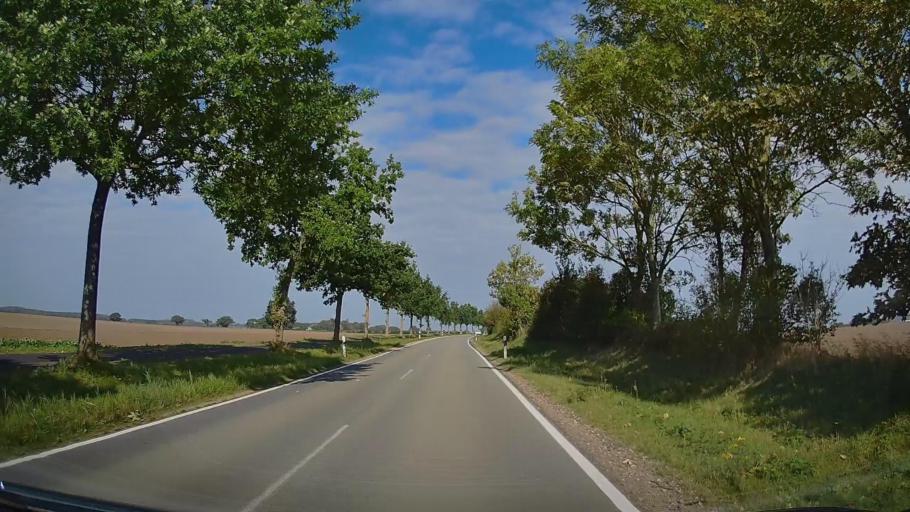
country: DE
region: Schleswig-Holstein
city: Oldenburg in Holstein
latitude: 54.3085
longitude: 10.8867
